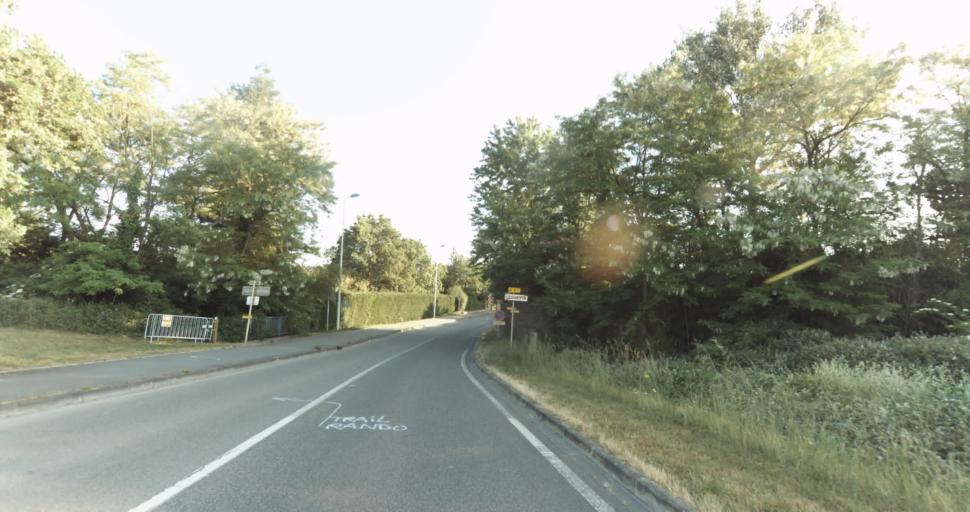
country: FR
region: Midi-Pyrenees
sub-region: Departement de la Haute-Garonne
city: Leguevin
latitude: 43.6075
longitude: 1.2343
